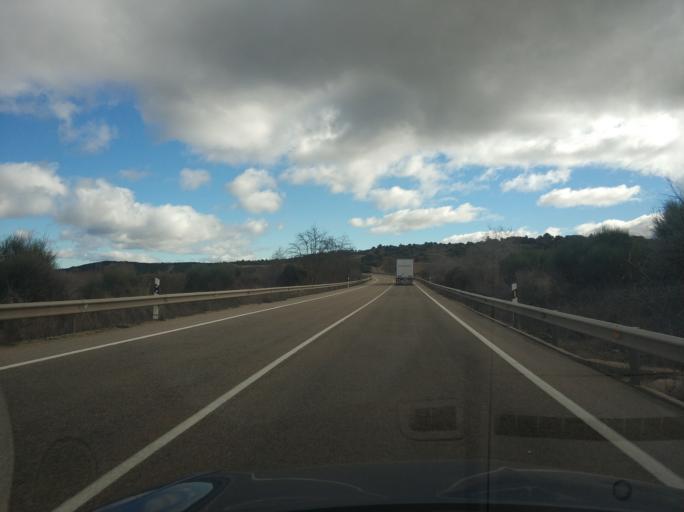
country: ES
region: Castille and Leon
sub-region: Provincia de Burgos
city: Vadocondes
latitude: 41.6295
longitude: -3.5585
